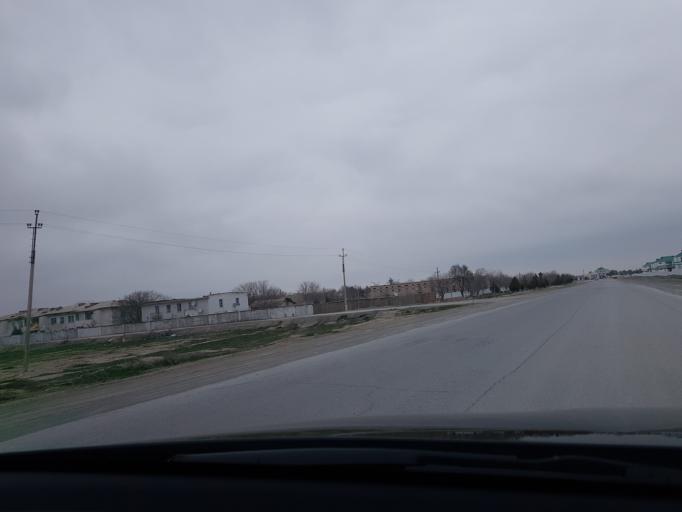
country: TM
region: Ahal
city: Arcabil
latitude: 38.1350
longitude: 57.9479
